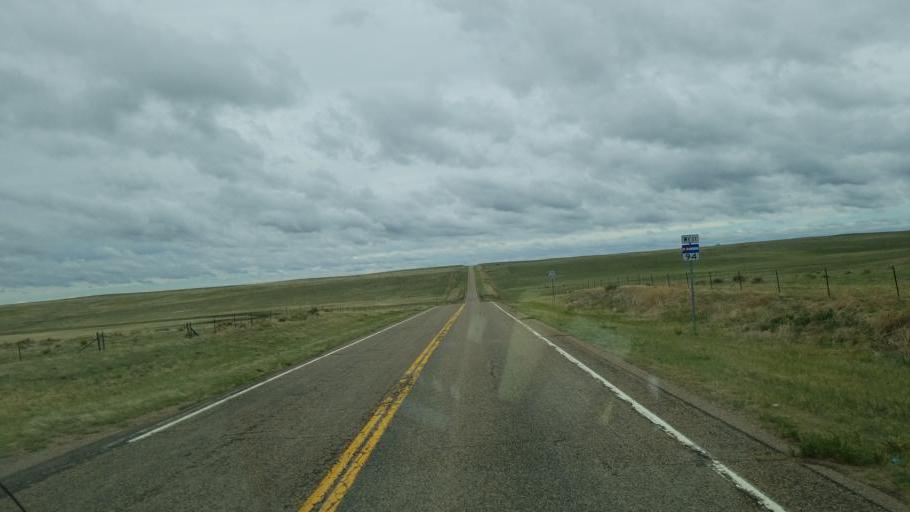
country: US
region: Colorado
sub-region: Lincoln County
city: Hugo
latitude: 38.8507
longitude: -103.5339
